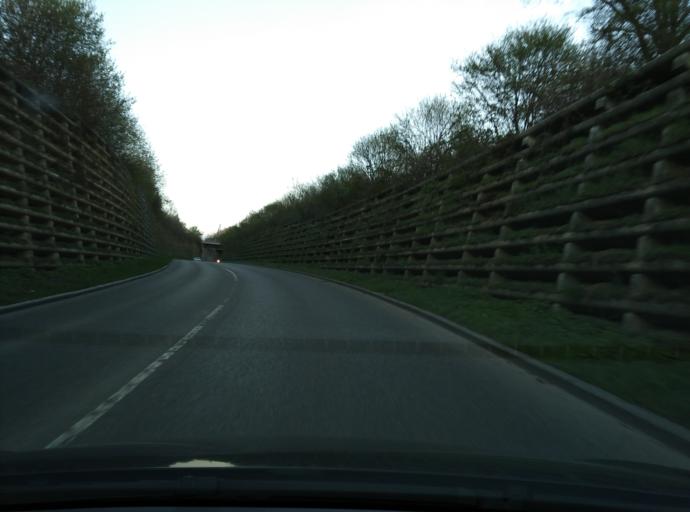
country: DE
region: Baden-Wuerttemberg
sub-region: Tuebingen Region
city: Metzingen
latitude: 48.5476
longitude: 9.2812
